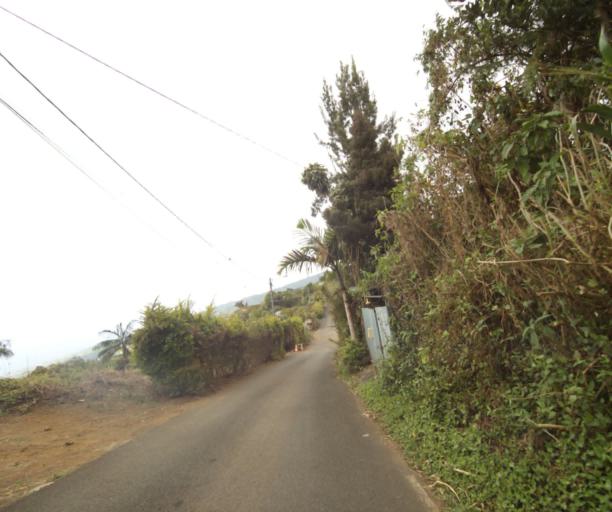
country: RE
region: Reunion
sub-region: Reunion
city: Saint-Paul
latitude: -21.0123
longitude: 55.3370
